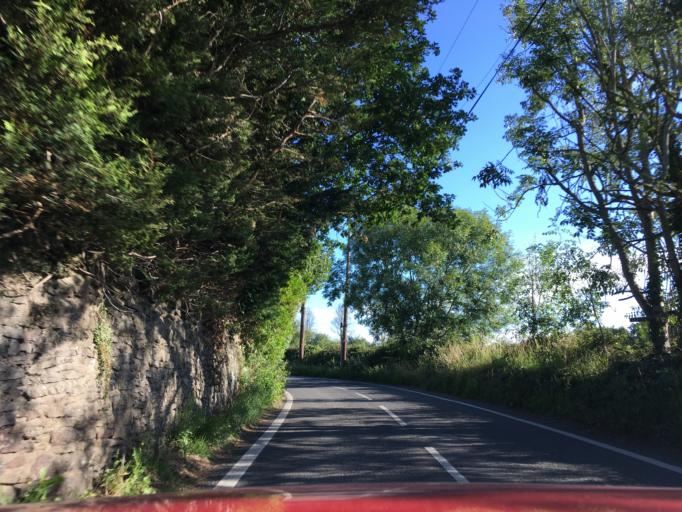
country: GB
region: England
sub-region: South Gloucestershire
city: Kingswood
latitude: 51.4348
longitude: -2.5120
